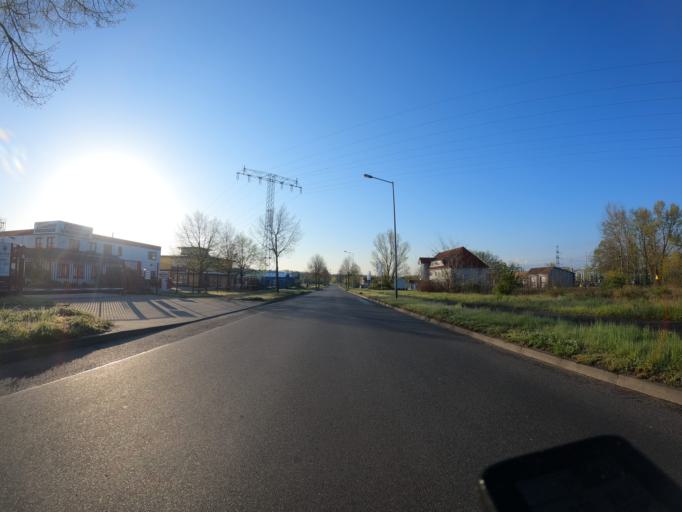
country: DE
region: Brandenburg
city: Neuenhagen
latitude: 52.5438
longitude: 13.7096
